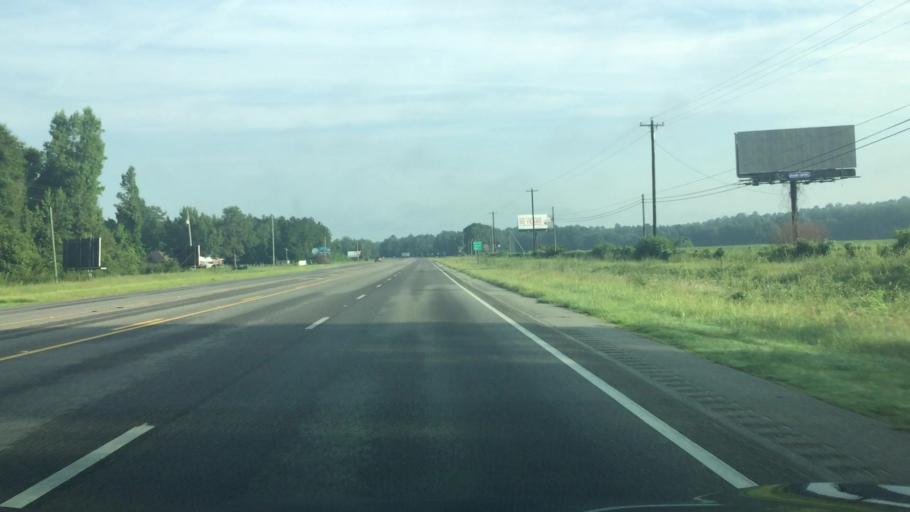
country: US
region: Alabama
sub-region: Covington County
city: Andalusia
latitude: 31.3393
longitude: -86.5223
